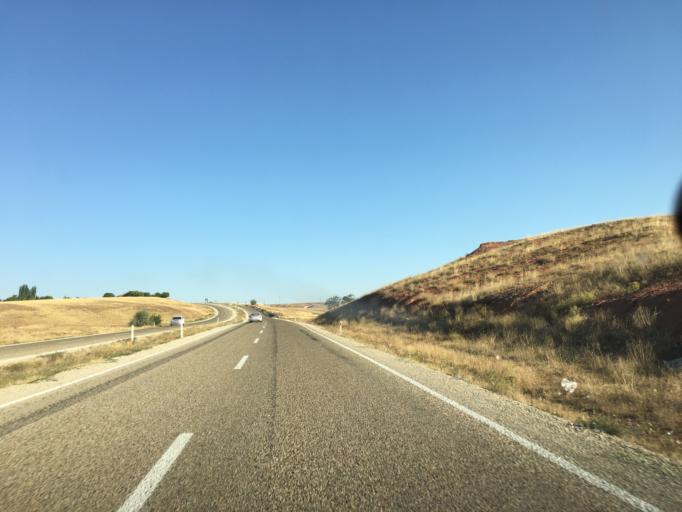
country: TR
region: Kirsehir
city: Mucur
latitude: 39.0132
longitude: 34.4605
